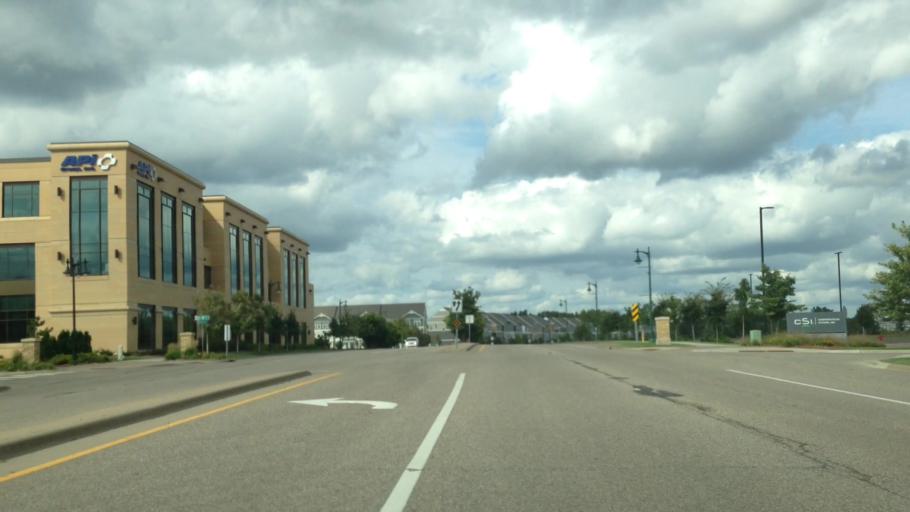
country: US
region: Minnesota
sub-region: Ramsey County
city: New Brighton
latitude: 45.0682
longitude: -93.1930
